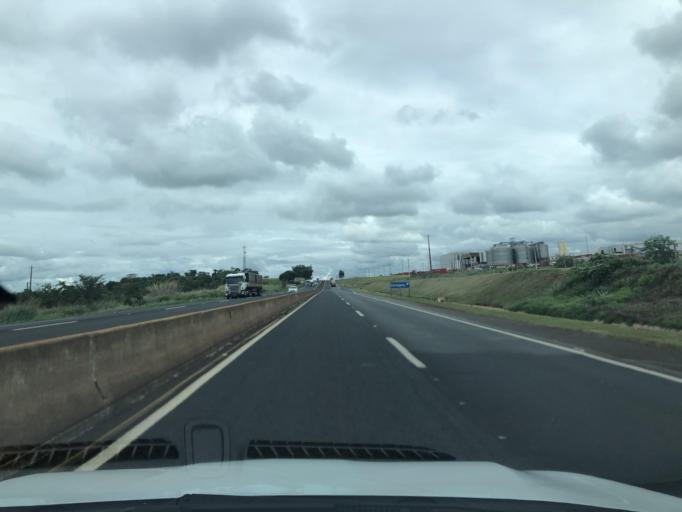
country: BR
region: Minas Gerais
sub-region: Uberaba
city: Uberaba
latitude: -19.8337
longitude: -47.8849
